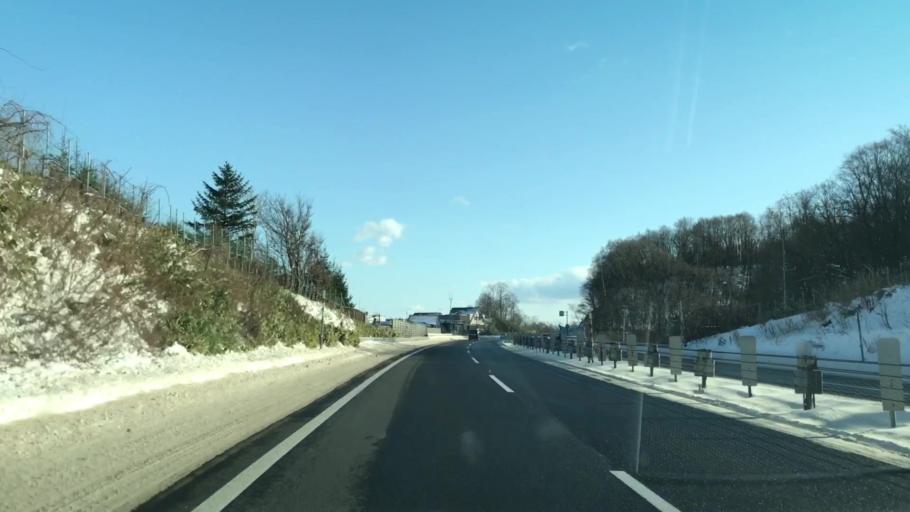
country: JP
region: Hokkaido
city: Sapporo
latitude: 43.1159
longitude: 141.2339
